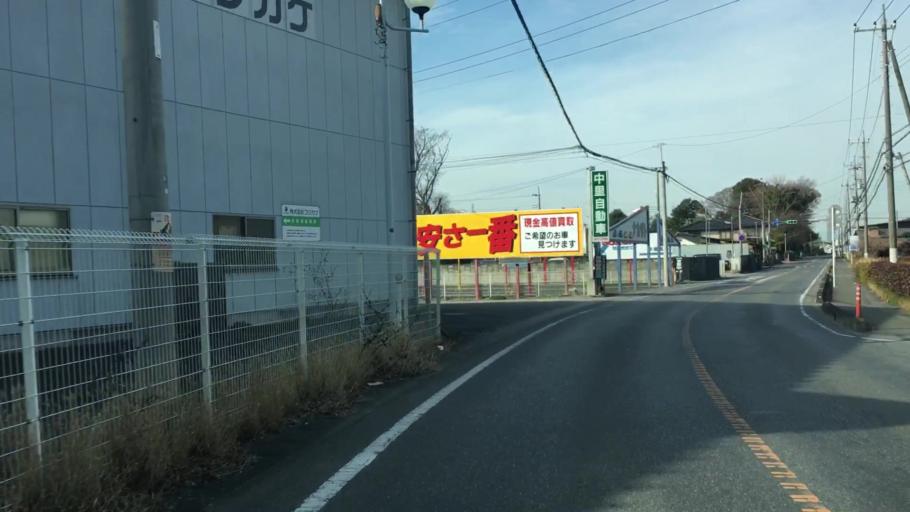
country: JP
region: Saitama
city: Menuma
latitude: 36.2476
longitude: 139.4347
